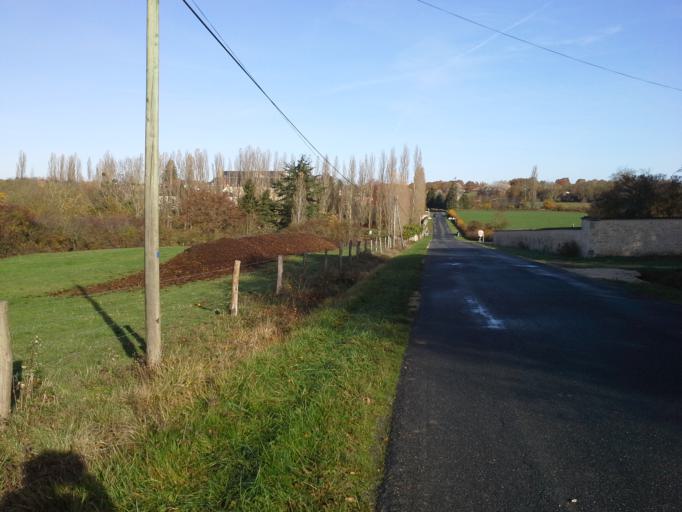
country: FR
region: Poitou-Charentes
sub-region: Departement de la Vienne
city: Pleumartin
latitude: 46.6375
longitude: 0.7539
